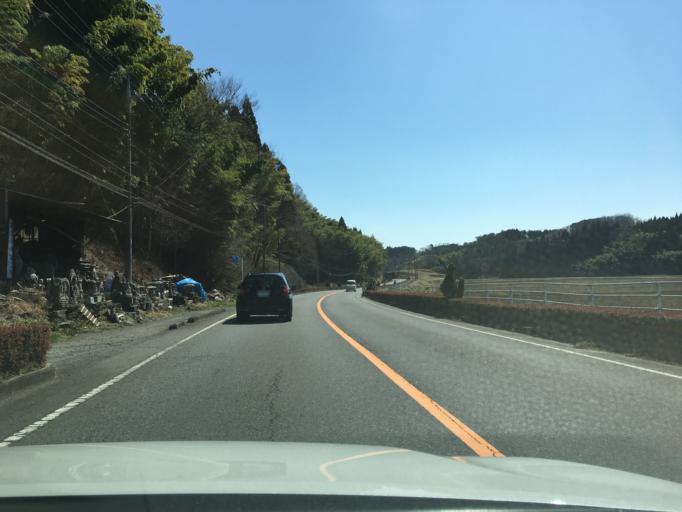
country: JP
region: Tochigi
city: Kuroiso
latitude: 37.0347
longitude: 140.1729
